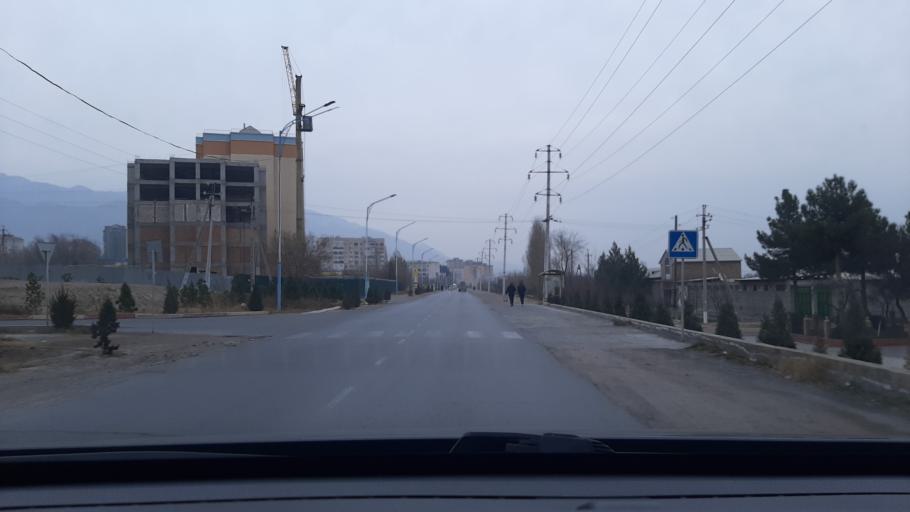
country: TJ
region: Viloyati Sughd
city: Khujand
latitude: 40.2823
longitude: 69.5866
